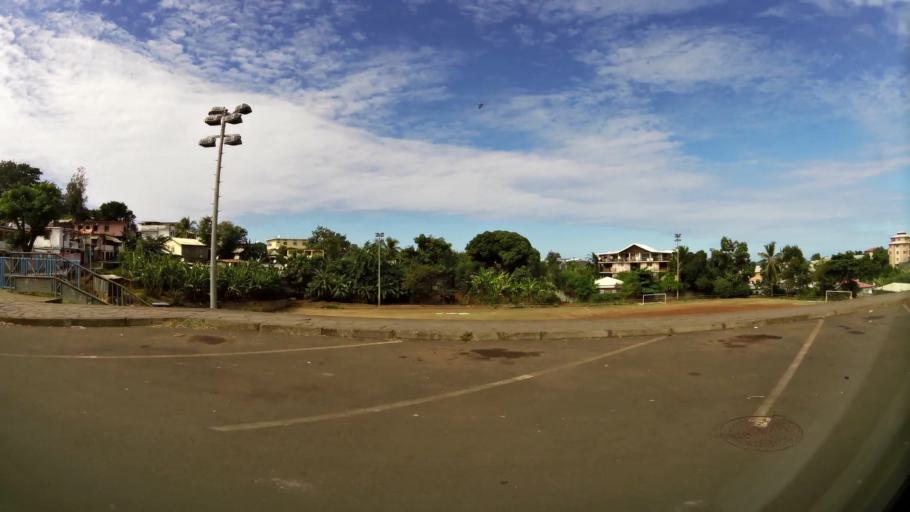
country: YT
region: Mamoudzou
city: Mamoudzou
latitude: -12.7813
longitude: 45.2275
